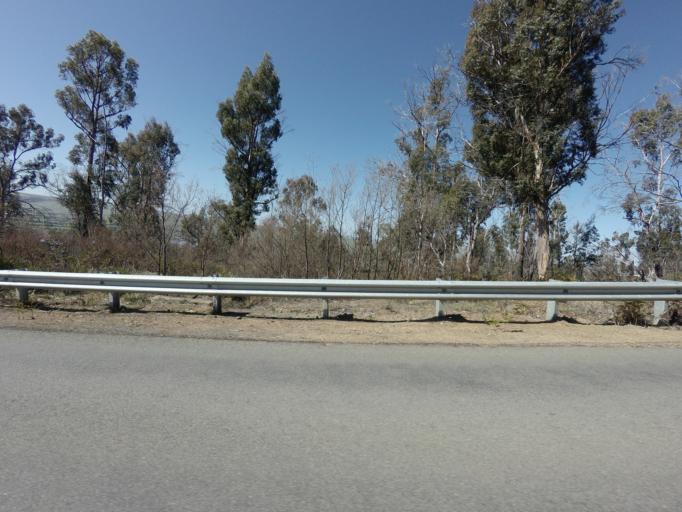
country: AU
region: Tasmania
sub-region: Derwent Valley
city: New Norfolk
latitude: -42.5488
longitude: 146.7142
